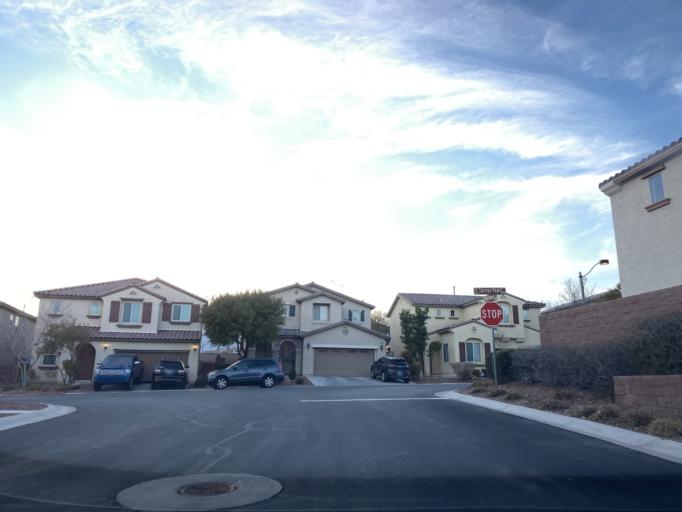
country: US
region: Nevada
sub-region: Clark County
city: Summerlin South
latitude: 36.3048
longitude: -115.3243
